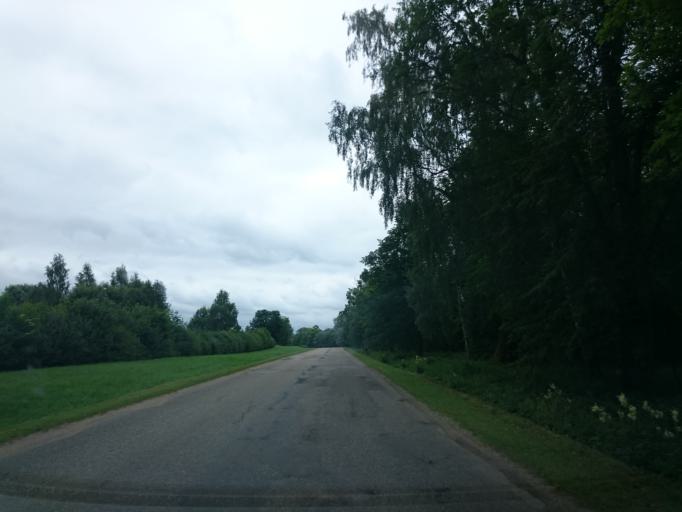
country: LV
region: Pavilostas
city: Pavilosta
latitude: 56.8791
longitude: 21.2135
